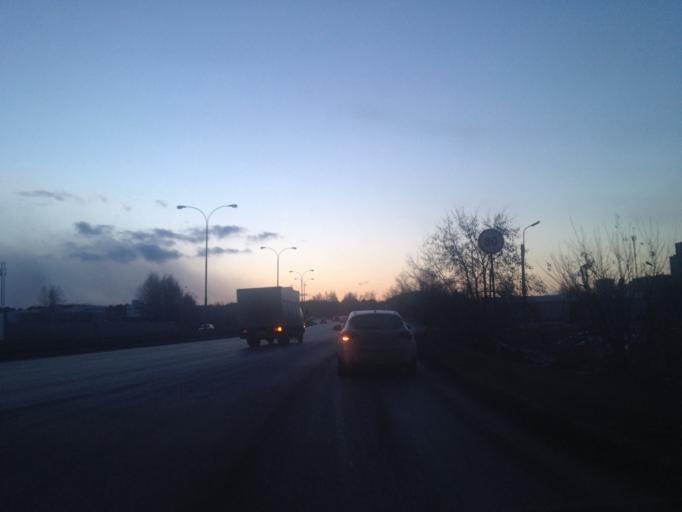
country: RU
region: Sverdlovsk
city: Yekaterinburg
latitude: 56.7900
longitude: 60.6137
